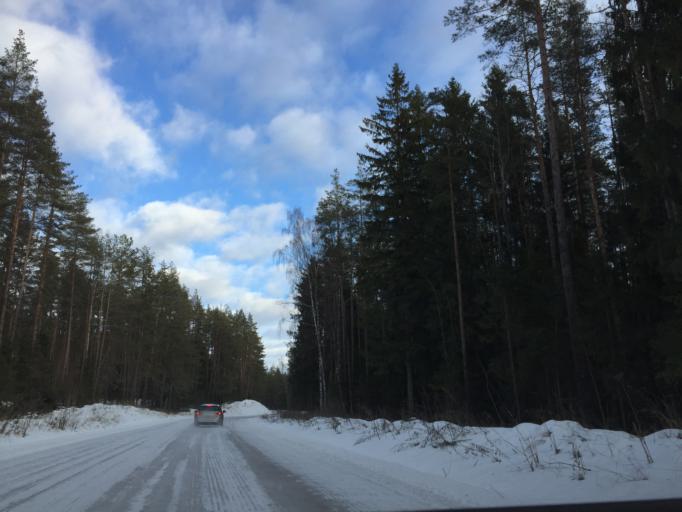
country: LV
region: Ogre
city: Jumprava
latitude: 56.5748
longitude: 24.9394
